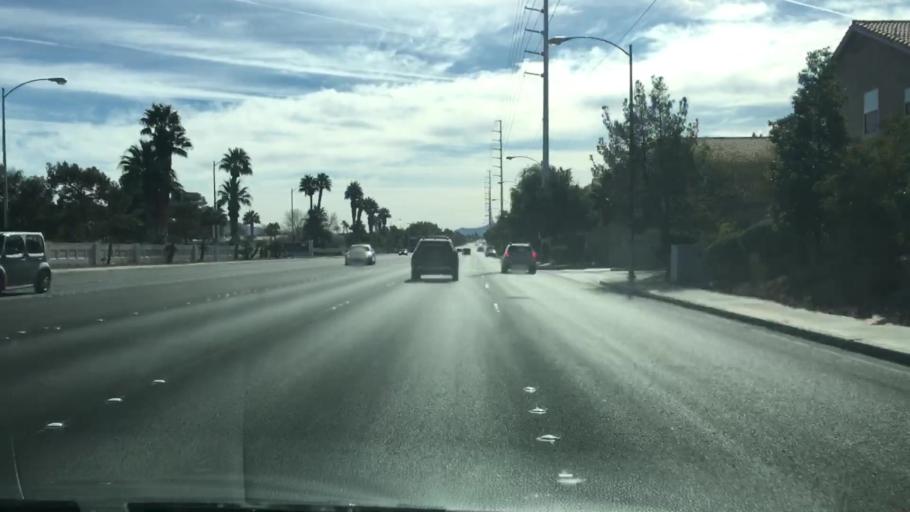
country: US
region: Nevada
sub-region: Clark County
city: Whitney
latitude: 36.0527
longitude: -115.1183
